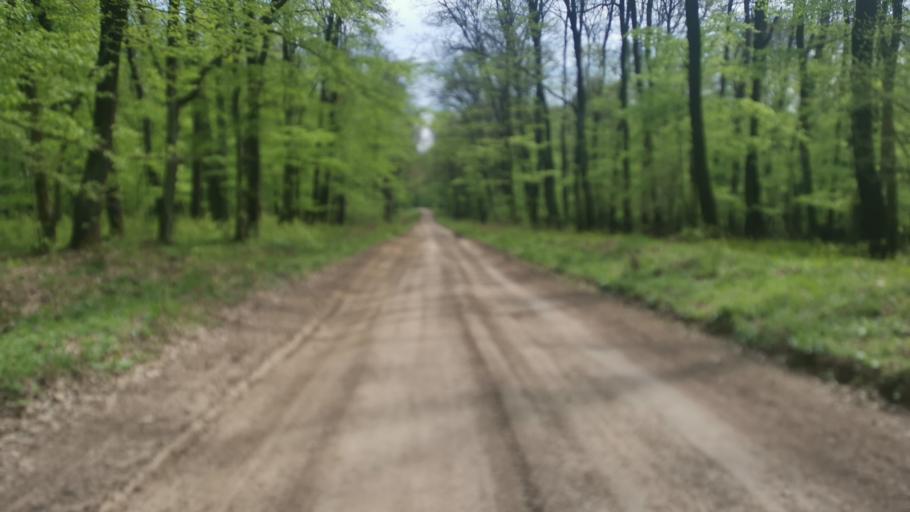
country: SK
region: Trnavsky
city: Smolenice
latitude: 48.5549
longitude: 17.4371
